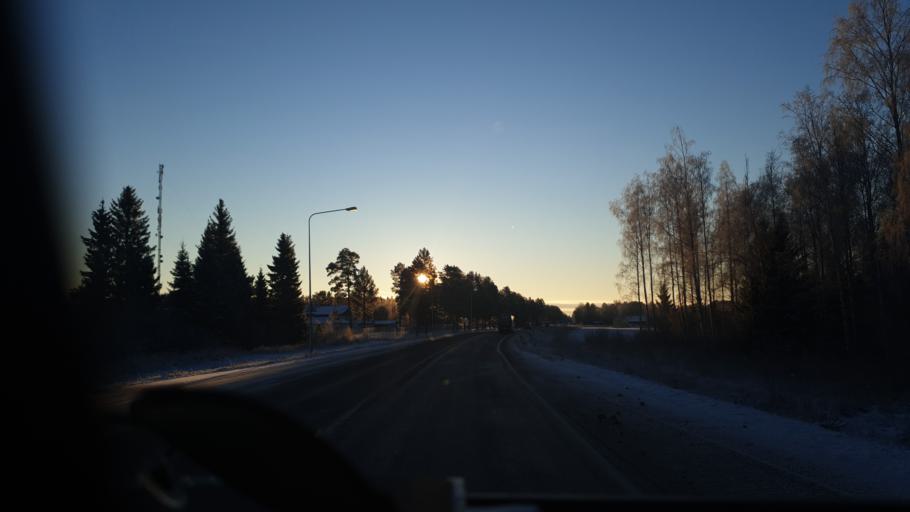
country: FI
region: Northern Ostrobothnia
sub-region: Ylivieska
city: Kalajoki
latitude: 64.2836
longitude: 23.9479
